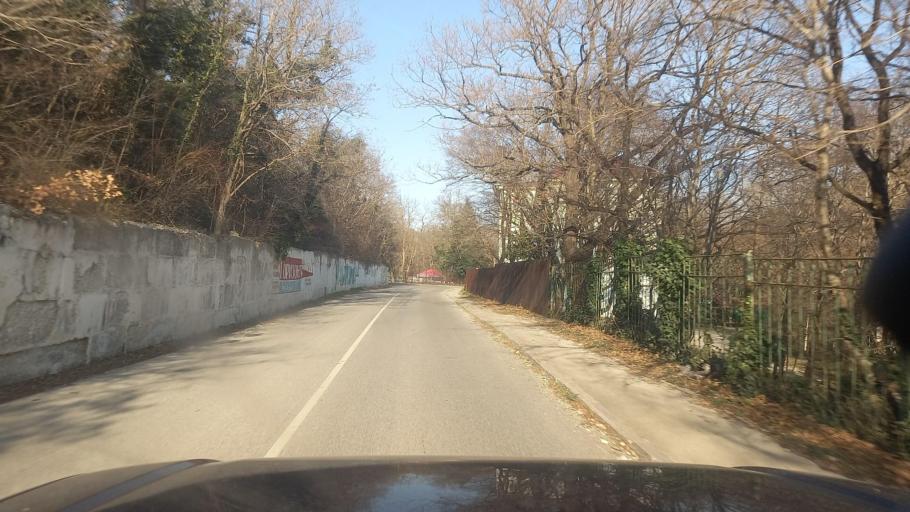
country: RU
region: Krasnodarskiy
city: Myskhako
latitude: 44.6641
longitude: 37.6849
